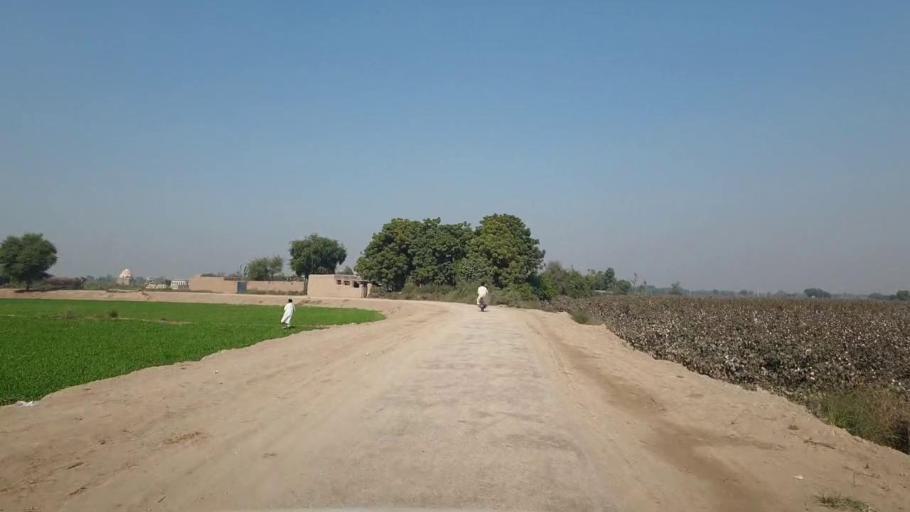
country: PK
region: Sindh
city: Bhan
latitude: 26.6403
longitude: 67.7174
